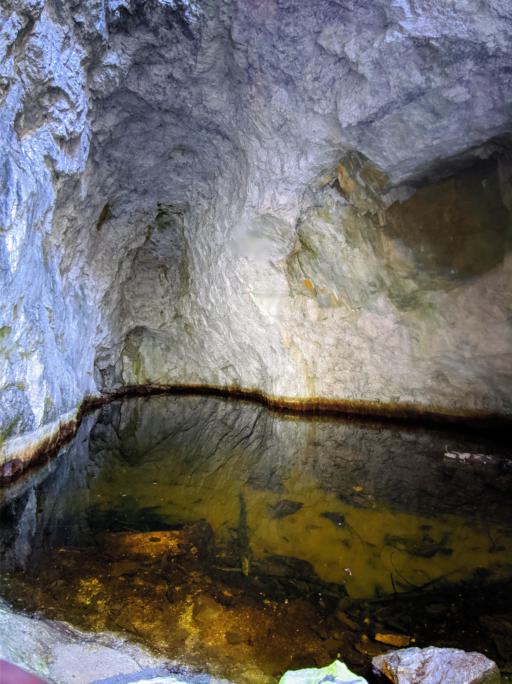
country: NO
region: Akershus
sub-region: Nesodden
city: Fagerstrand
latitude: 59.7669
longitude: 10.5872
